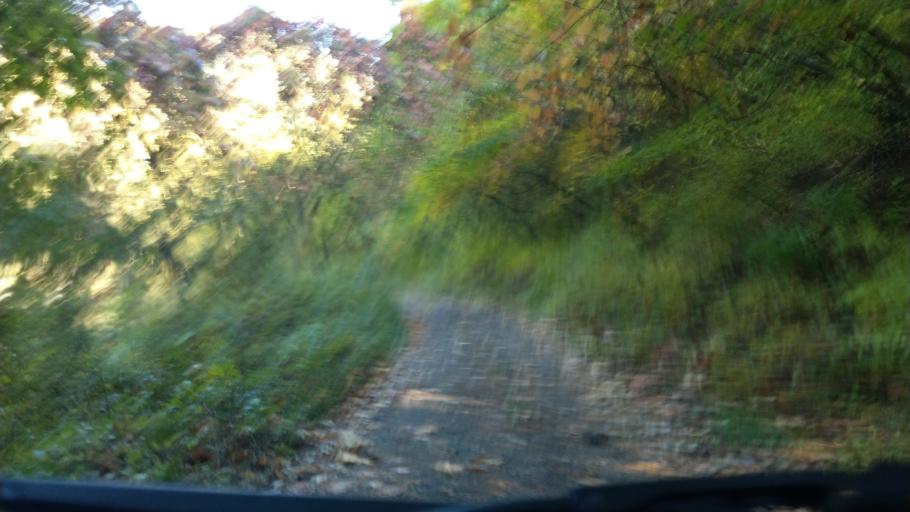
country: JP
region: Nagano
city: Komoro
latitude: 36.3762
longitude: 138.4300
